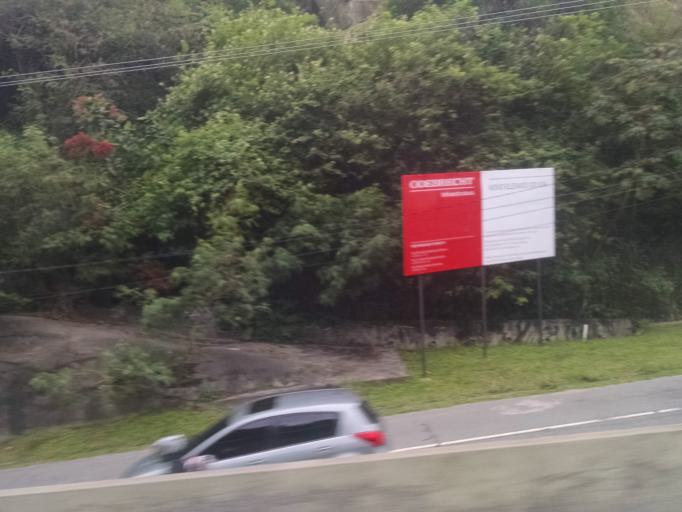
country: BR
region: Rio de Janeiro
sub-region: Rio De Janeiro
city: Rio de Janeiro
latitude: -23.0123
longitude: -43.2928
